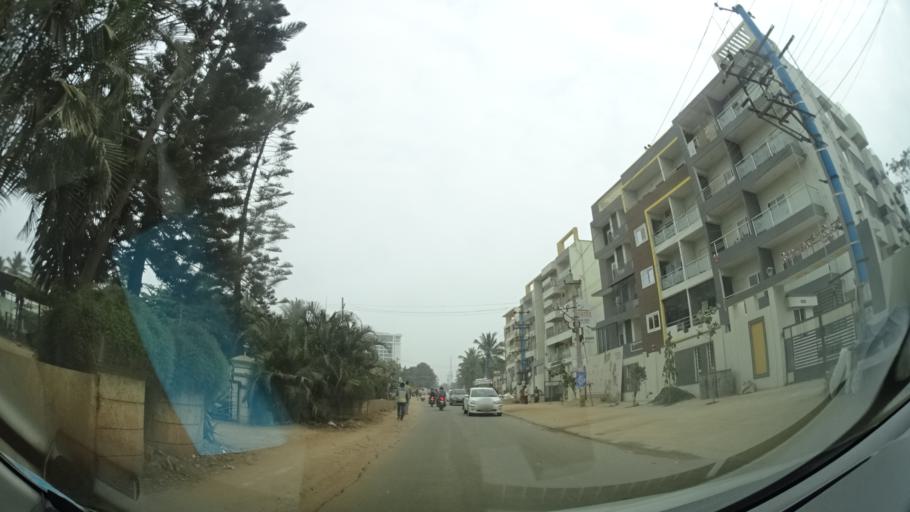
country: IN
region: Karnataka
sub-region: Bangalore Rural
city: Hoskote
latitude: 12.9586
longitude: 77.7319
